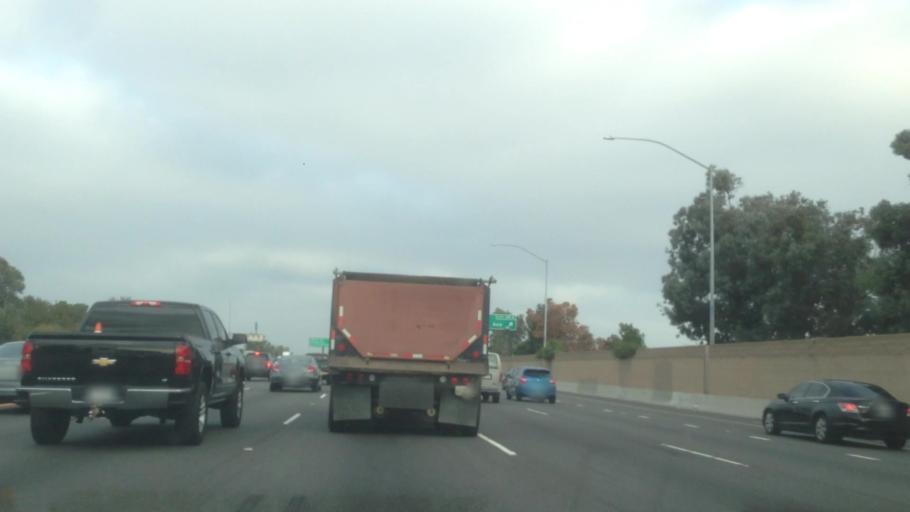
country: US
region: California
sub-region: Los Angeles County
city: Gardena
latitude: 33.8608
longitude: -118.2946
